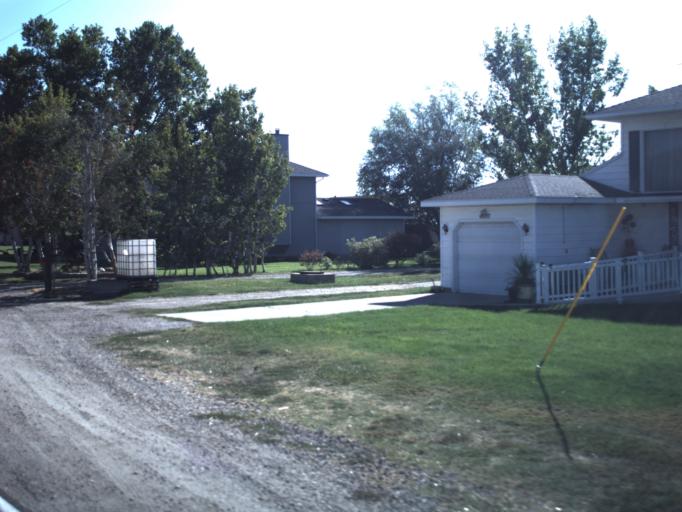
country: US
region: Utah
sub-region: Weber County
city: Hooper
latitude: 41.1848
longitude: -112.1227
